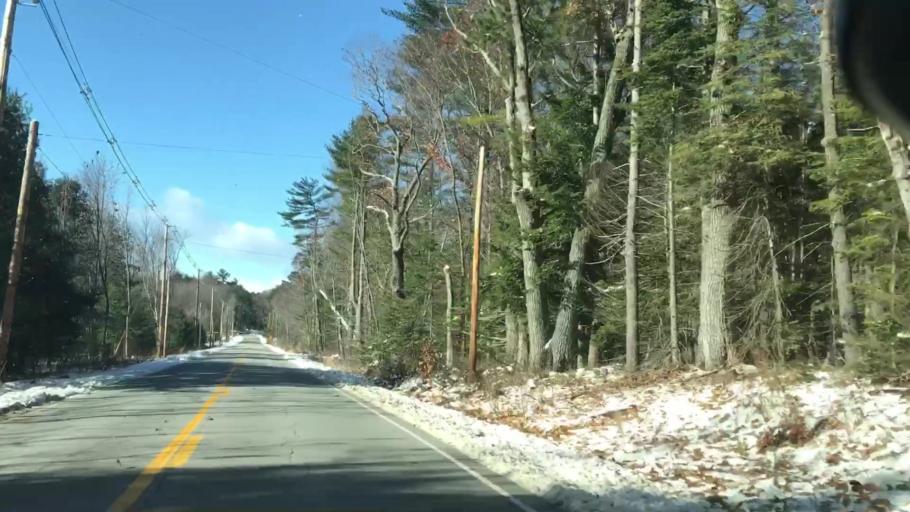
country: US
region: Maine
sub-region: Oxford County
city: Brownfield
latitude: 43.9650
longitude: -70.8692
